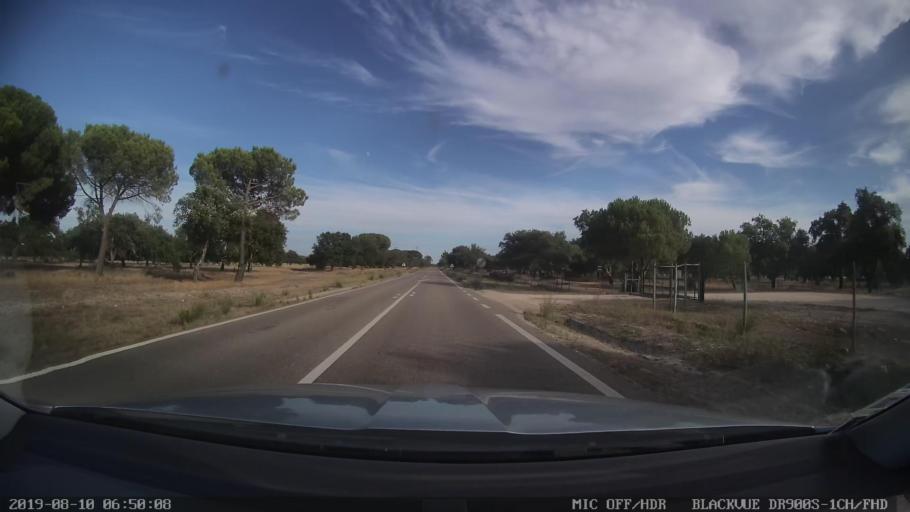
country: PT
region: Santarem
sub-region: Benavente
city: Benavente
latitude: 38.9097
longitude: -8.7635
